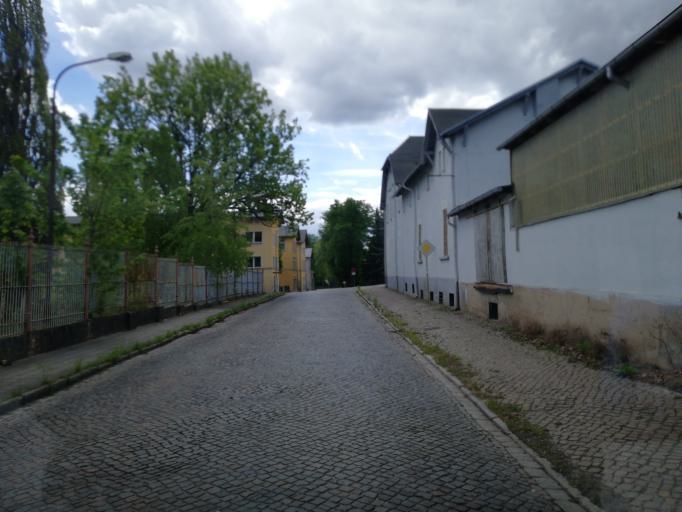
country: DE
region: Brandenburg
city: Lauchhammer
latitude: 51.5041
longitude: 13.7982
